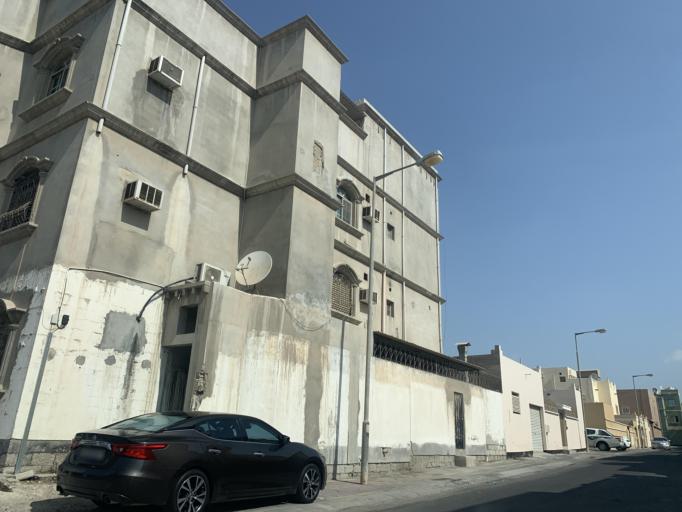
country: BH
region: Central Governorate
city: Madinat Hamad
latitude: 26.1283
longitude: 50.4997
